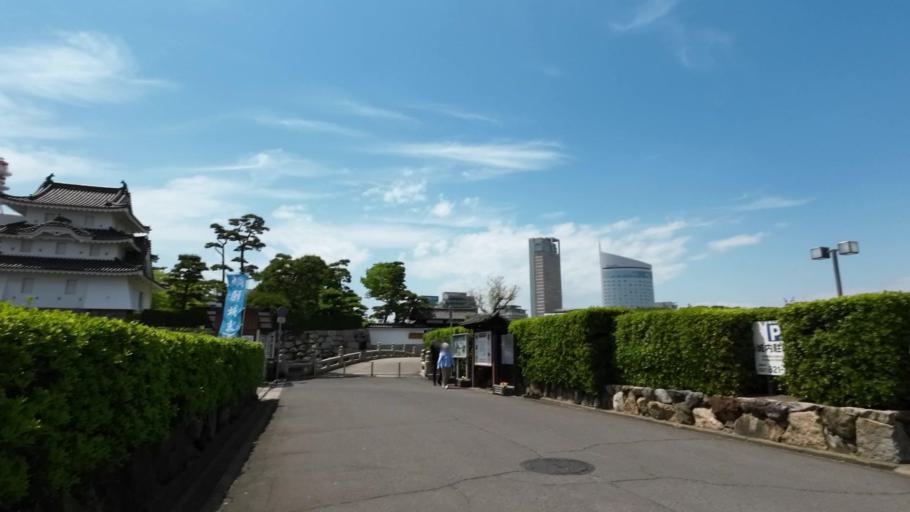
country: JP
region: Kagawa
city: Takamatsu-shi
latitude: 34.3488
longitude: 134.0529
